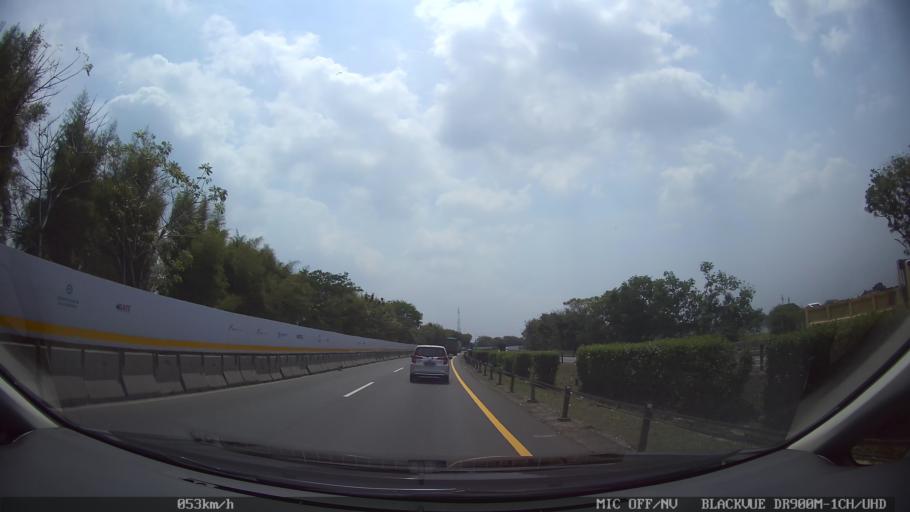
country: ID
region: Banten
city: Serang
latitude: -6.1291
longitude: 106.1951
